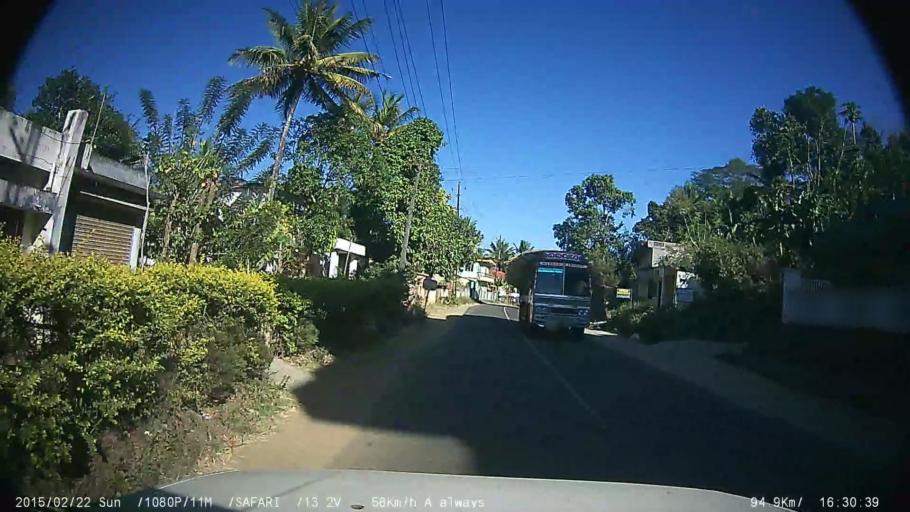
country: IN
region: Tamil Nadu
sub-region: Theni
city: Gudalur
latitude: 9.6099
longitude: 77.1589
